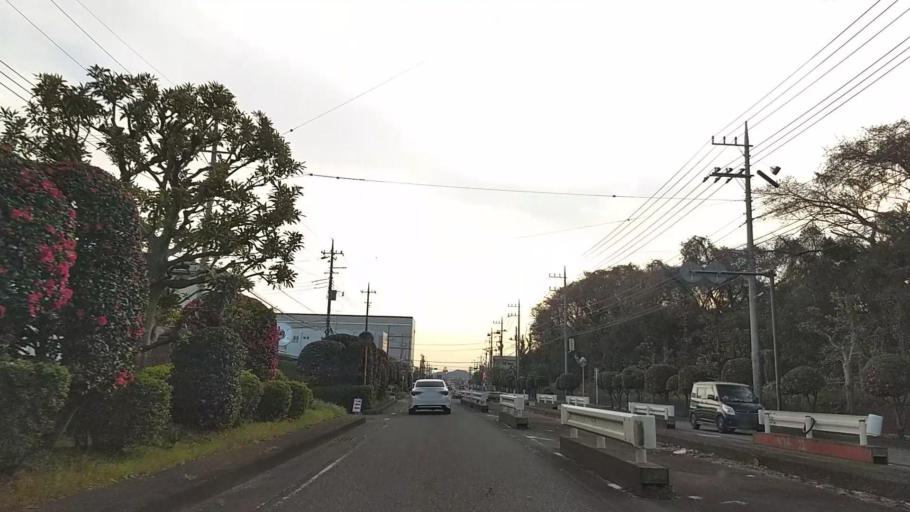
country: JP
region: Kanagawa
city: Atsugi
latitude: 35.4571
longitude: 139.3309
